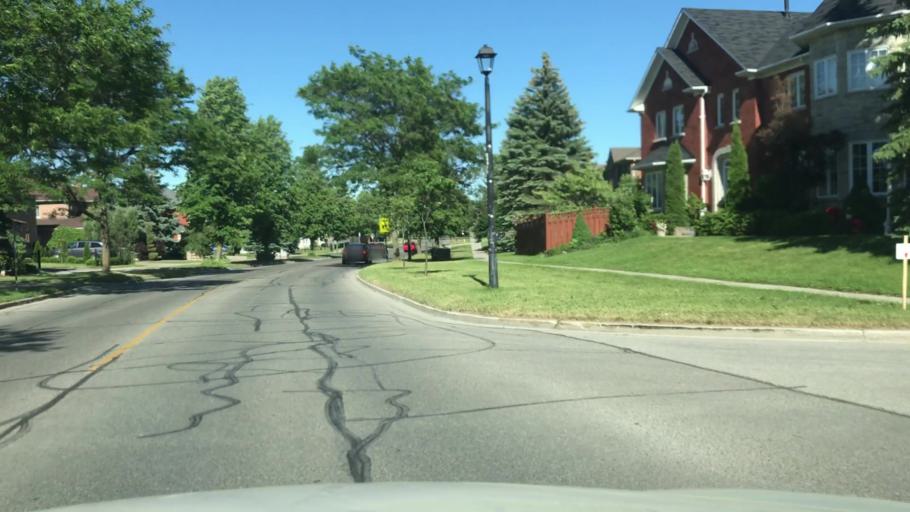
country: CA
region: Ontario
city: Newmarket
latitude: 44.0360
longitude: -79.4370
